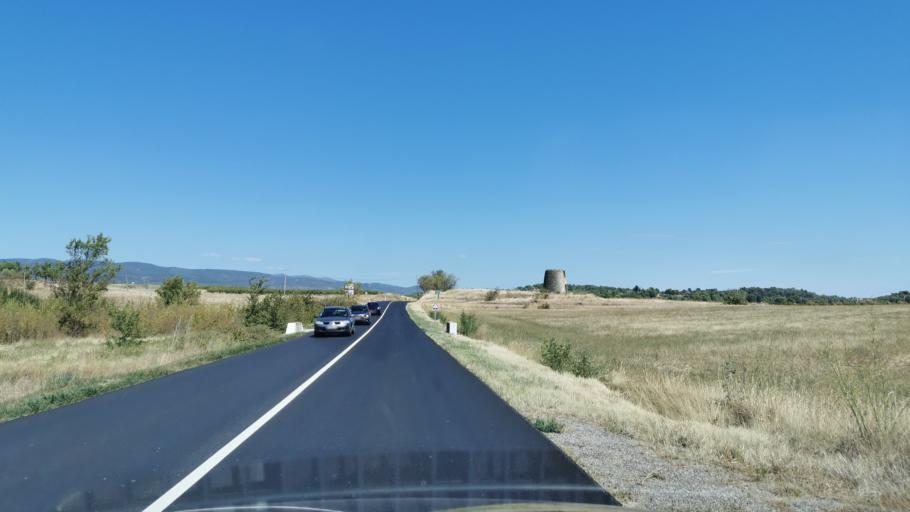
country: FR
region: Languedoc-Roussillon
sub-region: Departement de l'Aude
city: Conques-sur-Orbiel
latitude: 43.2764
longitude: 2.4272
